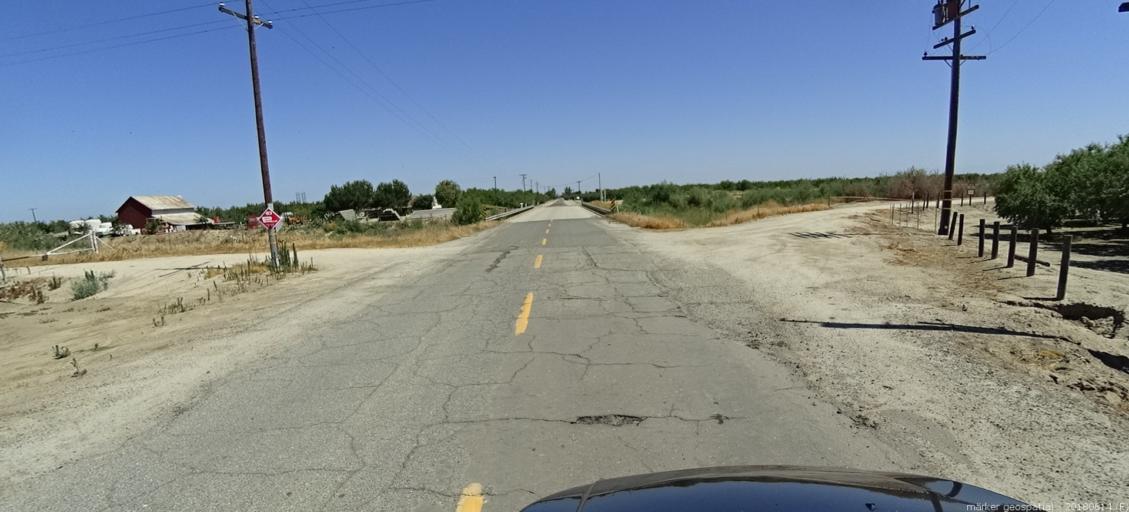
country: US
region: California
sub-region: Madera County
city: Fairmead
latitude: 36.9816
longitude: -120.1842
